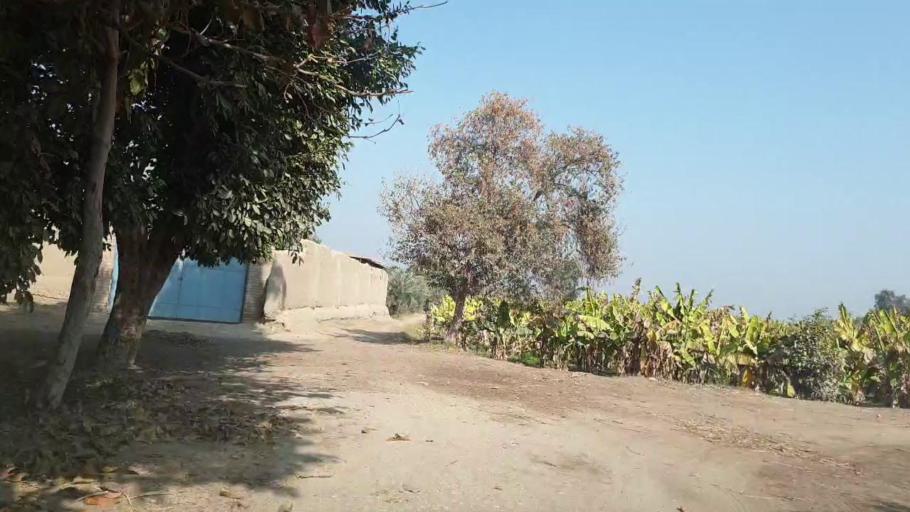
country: PK
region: Sindh
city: Matiari
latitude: 25.5485
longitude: 68.4980
